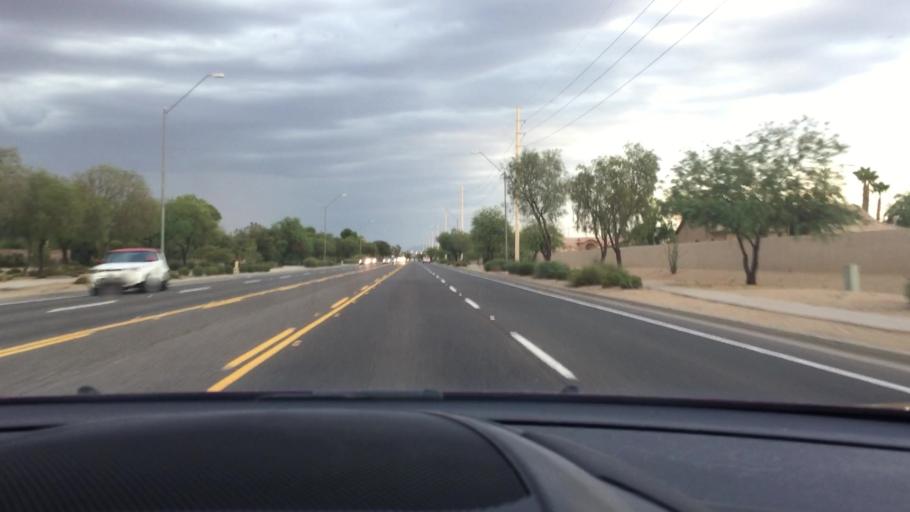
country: US
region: Arizona
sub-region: Maricopa County
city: Sun City
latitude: 33.6672
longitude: -112.2452
